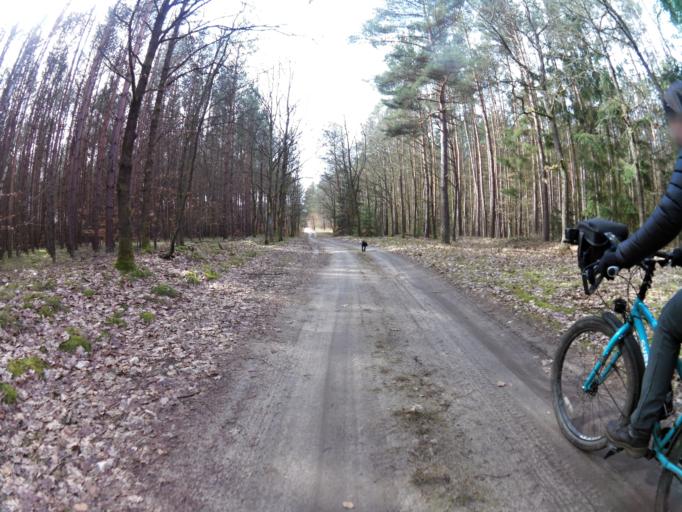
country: PL
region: West Pomeranian Voivodeship
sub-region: Powiat mysliborski
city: Mysliborz
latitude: 52.8625
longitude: 14.8443
